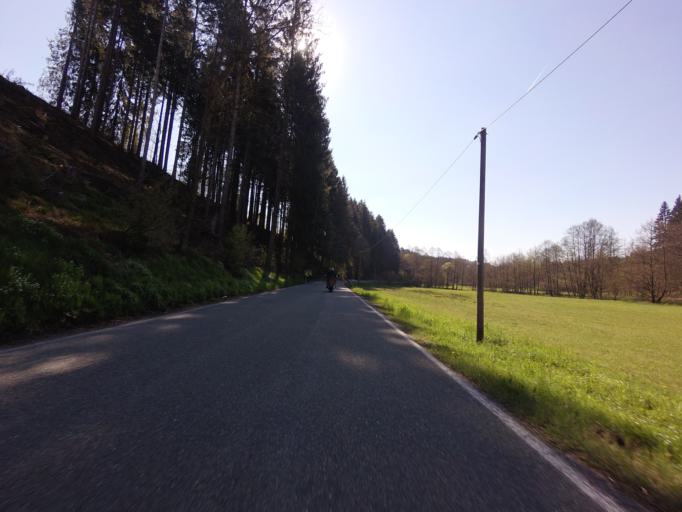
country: DE
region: North Rhine-Westphalia
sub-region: Regierungsbezirk Arnsberg
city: Herscheid
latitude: 51.1022
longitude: 7.7453
